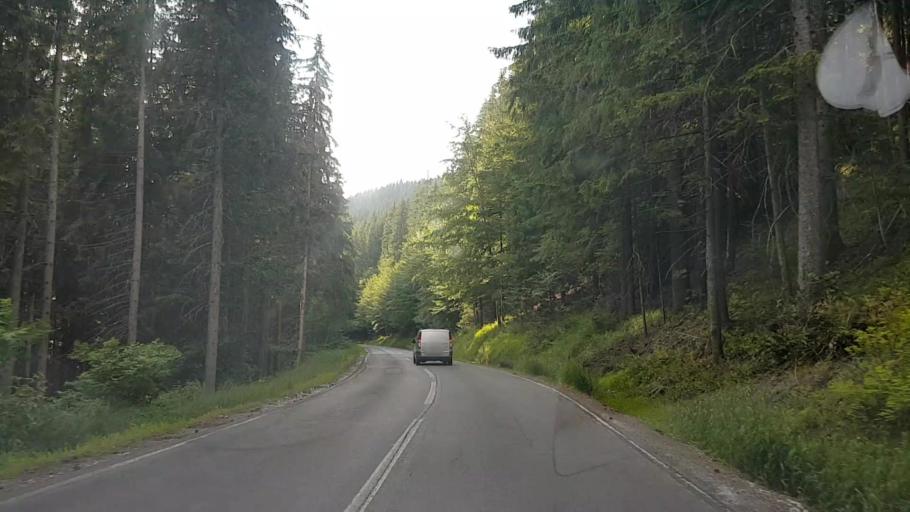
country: RO
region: Harghita
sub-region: Comuna Varsag
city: Varsag
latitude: 46.6638
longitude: 25.3152
